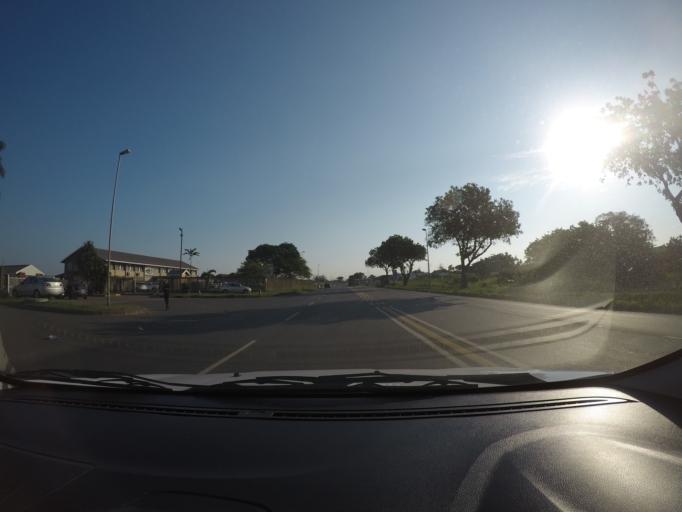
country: ZA
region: KwaZulu-Natal
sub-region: uThungulu District Municipality
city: Richards Bay
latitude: -28.7585
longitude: 32.0244
